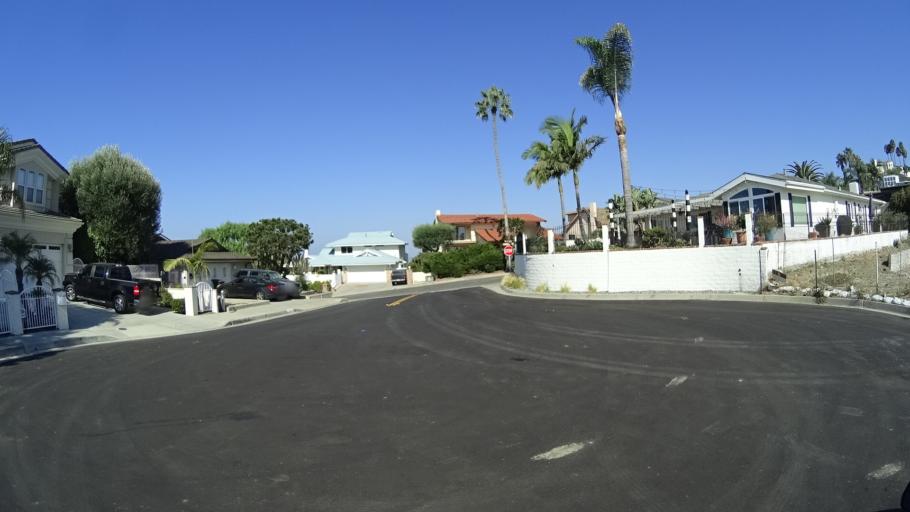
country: US
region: California
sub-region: Orange County
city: San Clemente
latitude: 33.4234
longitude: -117.6045
